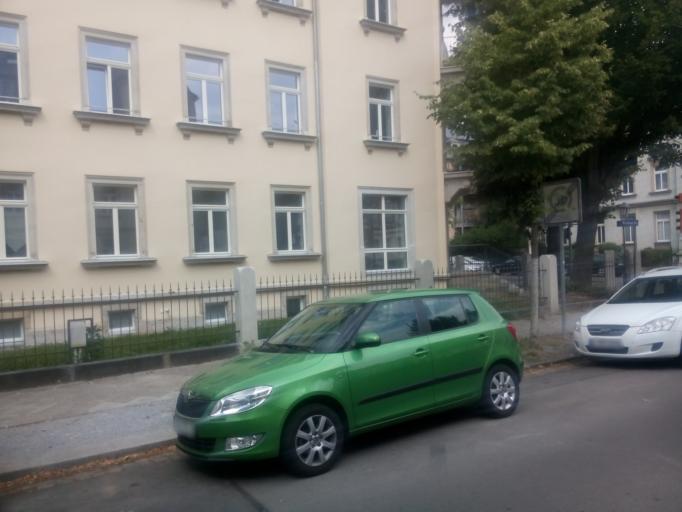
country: DE
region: Saxony
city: Albertstadt
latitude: 51.0445
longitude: 13.7966
